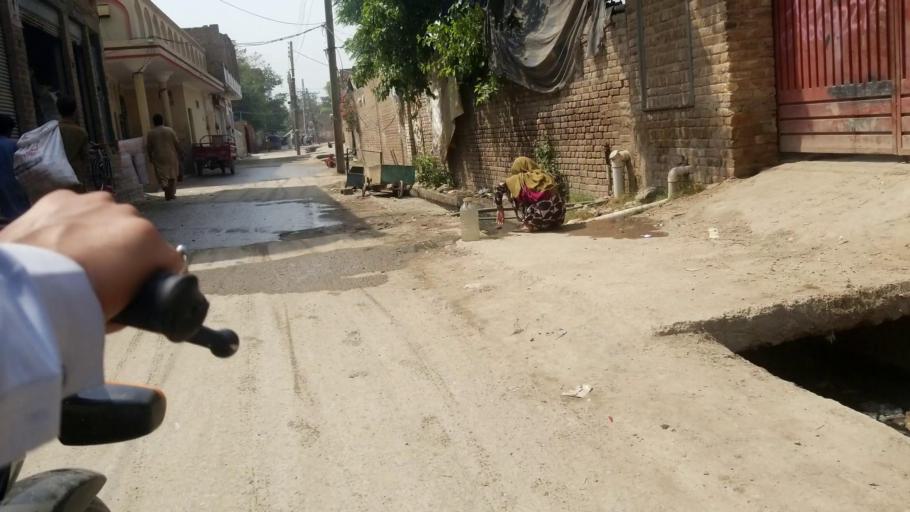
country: PK
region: Khyber Pakhtunkhwa
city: Peshawar
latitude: 33.9852
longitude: 71.5400
